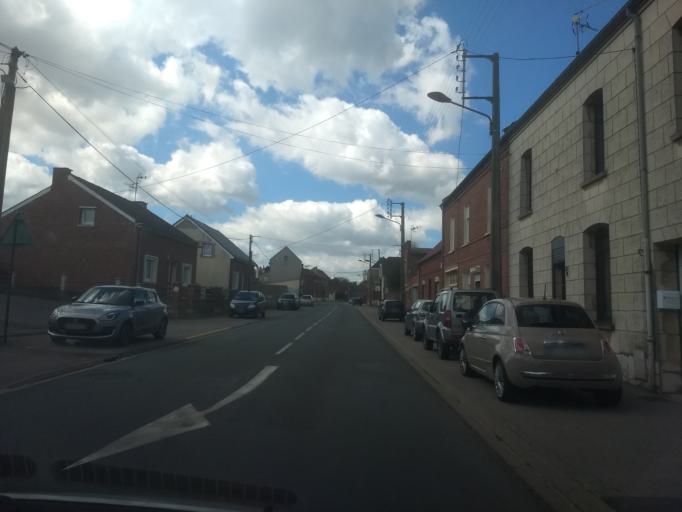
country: FR
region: Nord-Pas-de-Calais
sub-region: Departement du Pas-de-Calais
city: Bailleul-Sir-Berthoult
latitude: 50.3387
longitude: 2.8499
